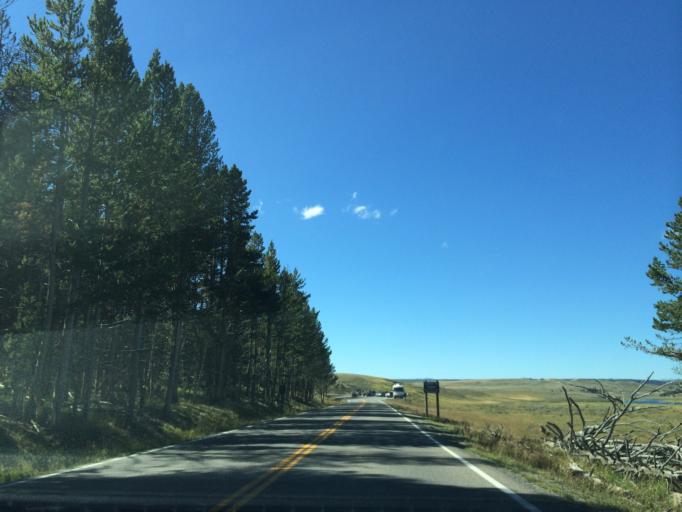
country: US
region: Montana
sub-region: Gallatin County
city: West Yellowstone
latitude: 44.6295
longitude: -110.4371
